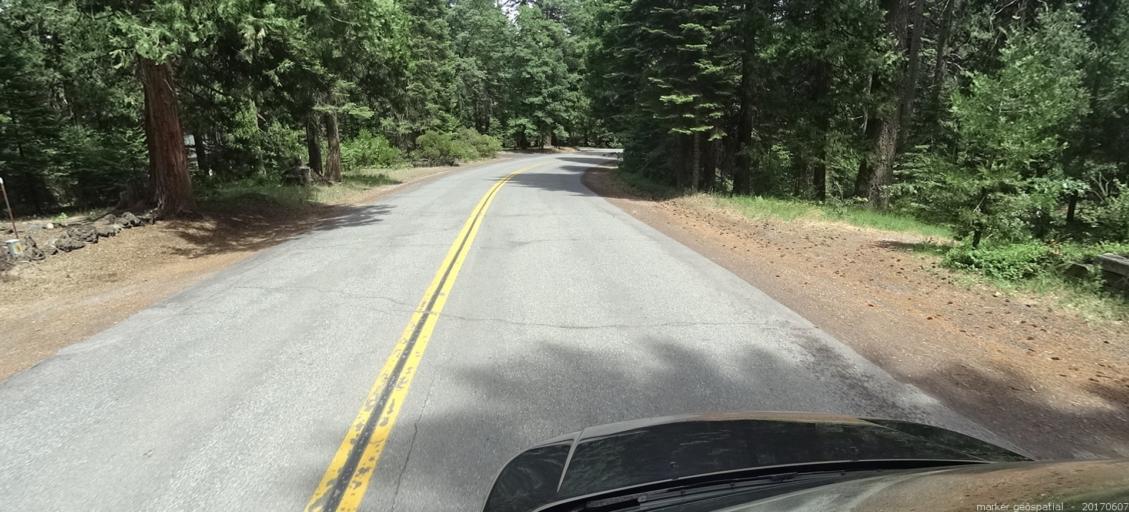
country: US
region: California
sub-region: Siskiyou County
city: Mount Shasta
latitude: 41.3320
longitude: -122.3537
